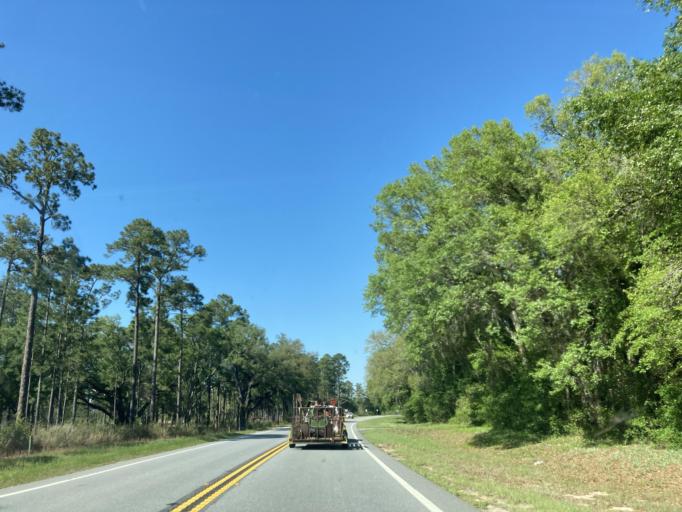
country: US
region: Georgia
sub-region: Baker County
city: Newton
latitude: 31.4326
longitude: -84.2774
